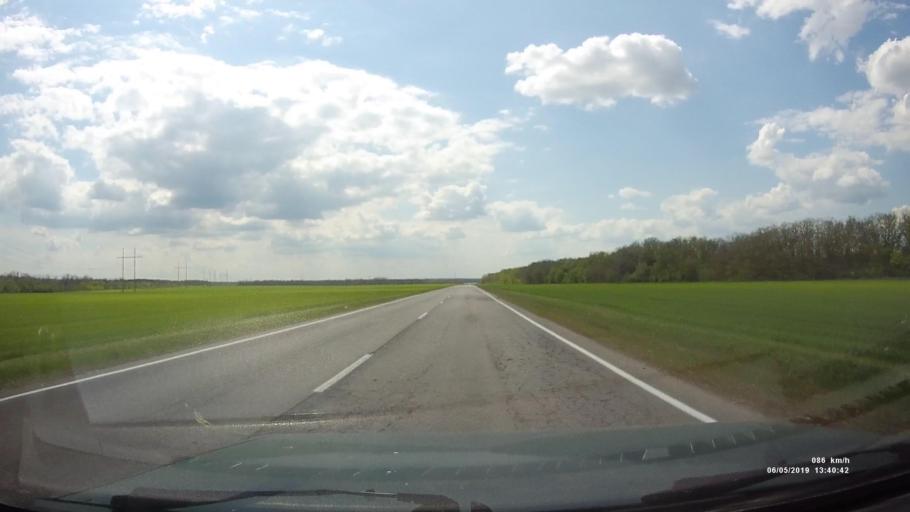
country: RU
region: Rostov
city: Ust'-Donetskiy
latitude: 47.6660
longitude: 40.6896
